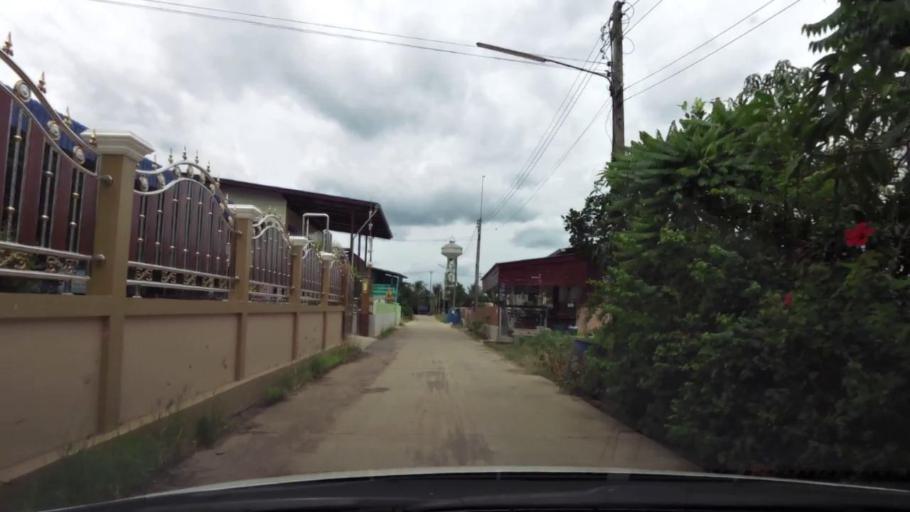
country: TH
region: Samut Sakhon
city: Ban Phaeo
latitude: 13.5738
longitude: 100.0313
